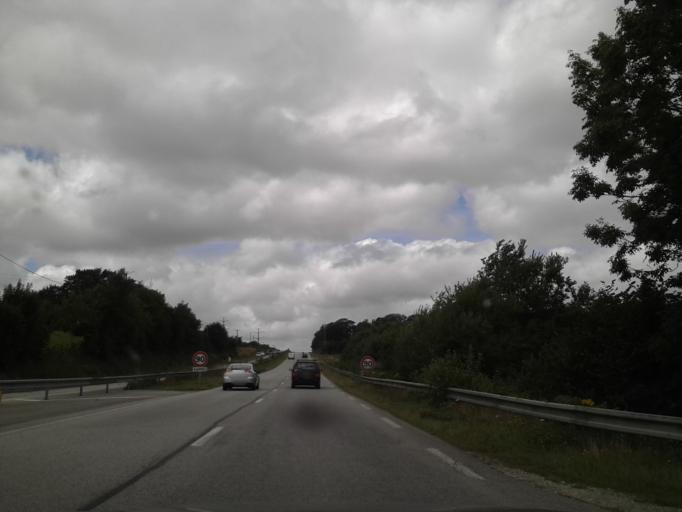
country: FR
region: Lower Normandy
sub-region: Departement de la Manche
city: La Glacerie
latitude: 49.5796
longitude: -1.5847
